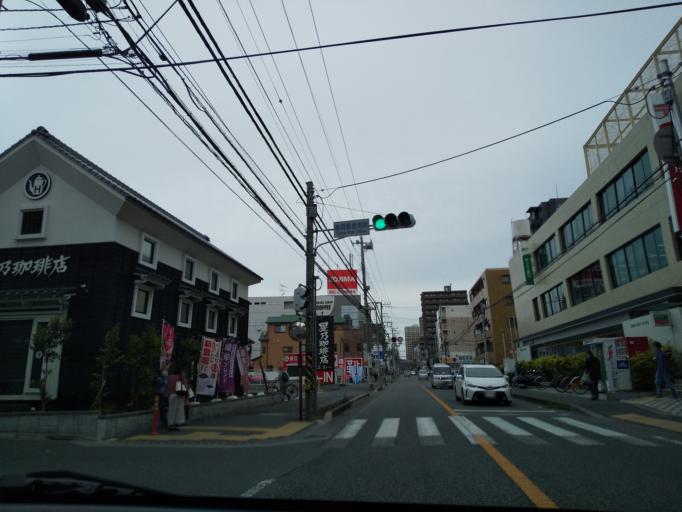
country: JP
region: Kanagawa
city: Zama
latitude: 35.5099
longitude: 139.4163
